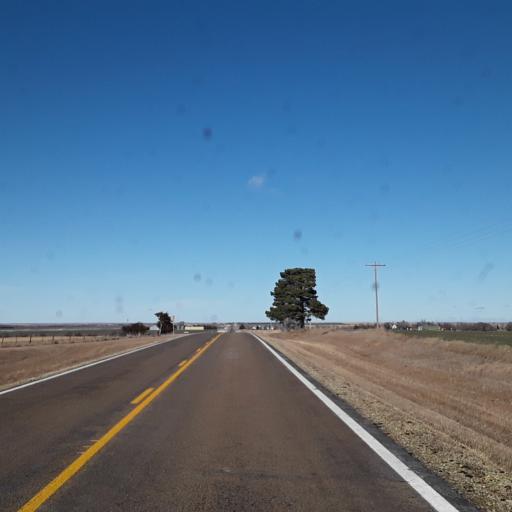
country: US
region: Kansas
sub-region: Mitchell County
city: Beloit
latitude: 39.3467
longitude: -98.1161
